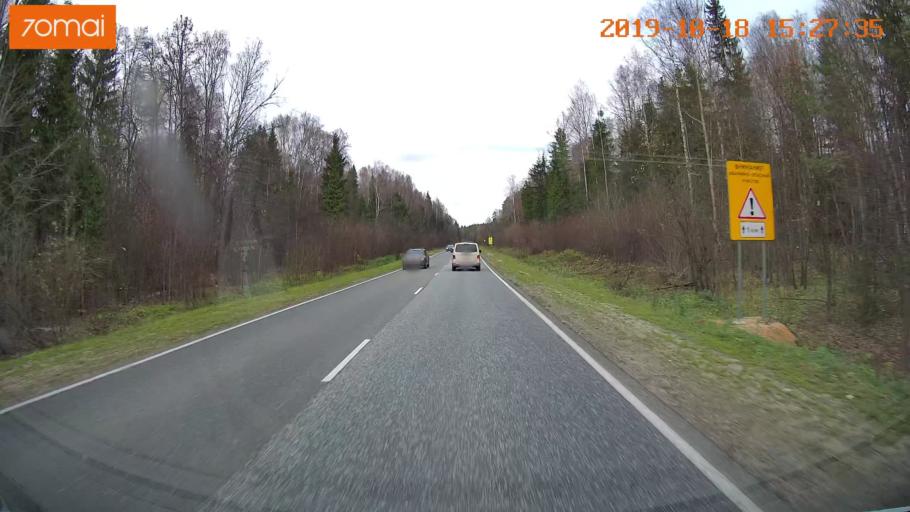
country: RU
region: Vladimir
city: Anopino
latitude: 55.7552
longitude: 40.6715
